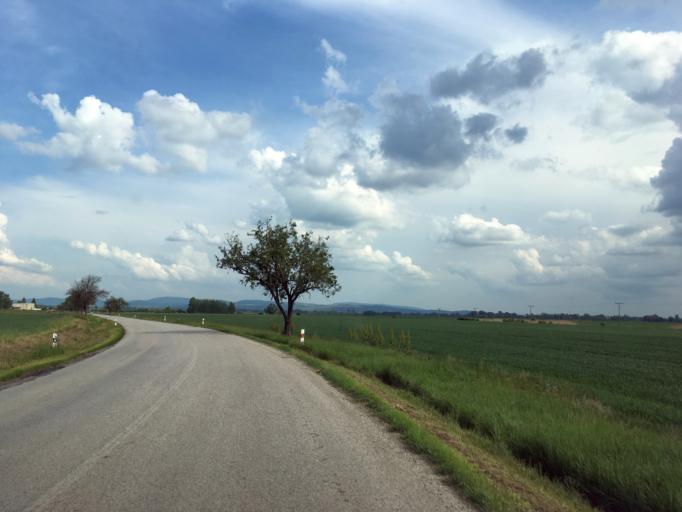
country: HU
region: Komarom-Esztergom
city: Almasfuzito
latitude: 47.7914
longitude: 18.2558
